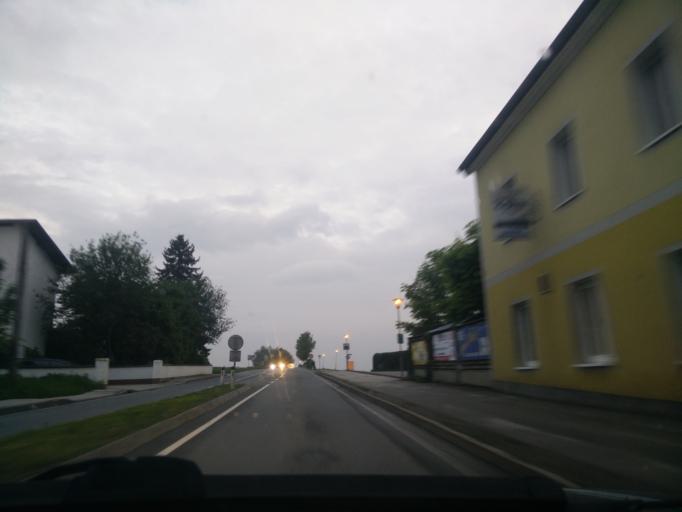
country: AT
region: Salzburg
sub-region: Politischer Bezirk Salzburg-Umgebung
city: Elixhausen
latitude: 47.8804
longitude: 13.0653
